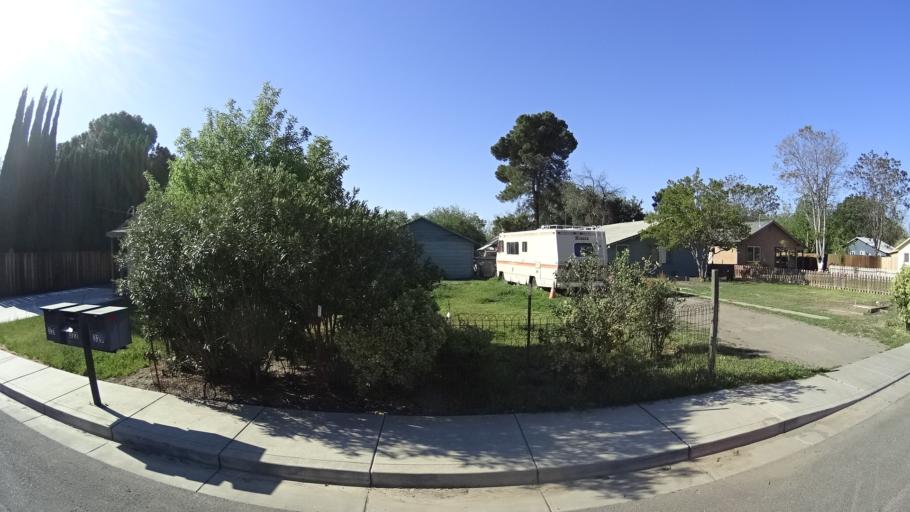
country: US
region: California
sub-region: Glenn County
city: Orland
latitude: 39.7426
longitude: -122.1933
